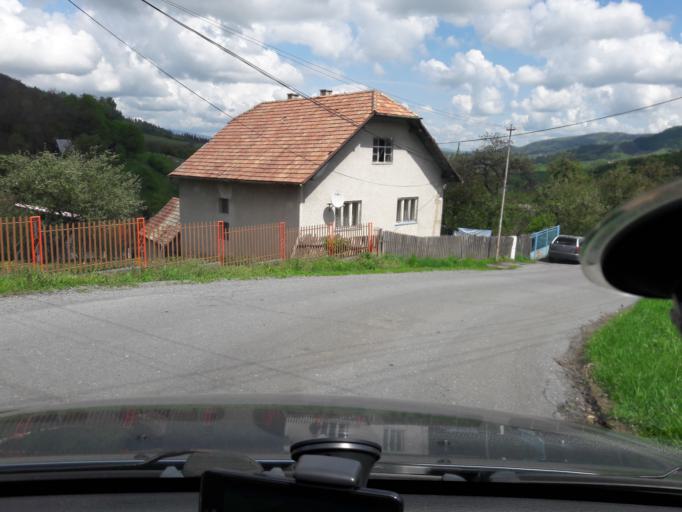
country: SK
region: Banskobystricky
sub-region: Okres Banska Bystrica
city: Zvolen
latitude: 48.4934
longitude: 19.2750
